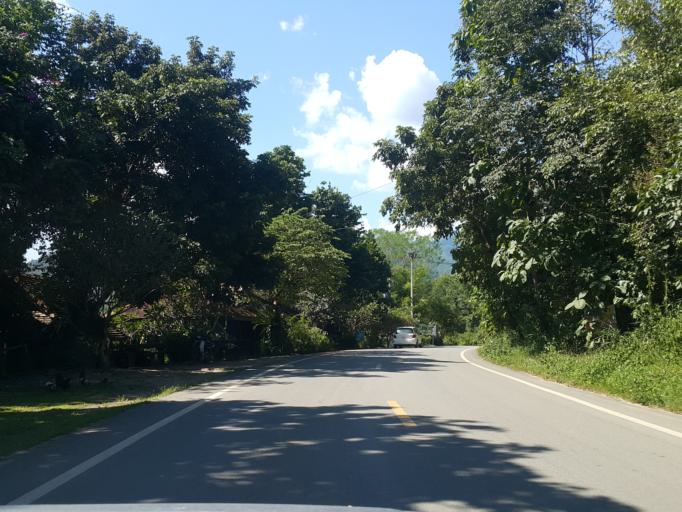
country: TH
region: Chiang Mai
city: Mae Taeng
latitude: 19.1988
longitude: 98.8928
